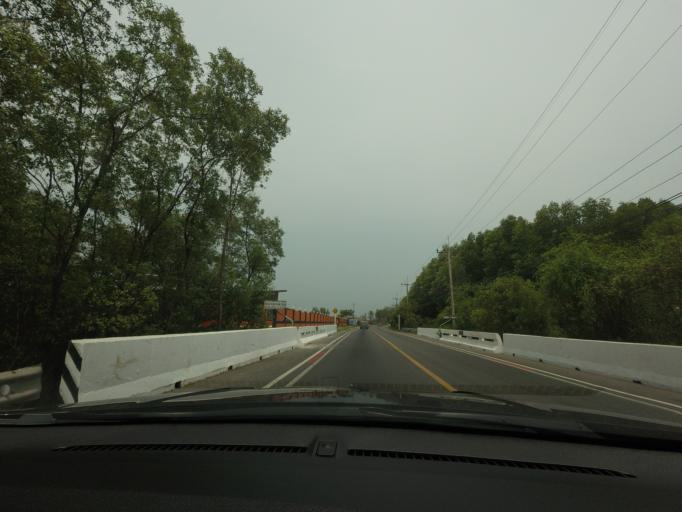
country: TH
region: Phetchaburi
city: Ban Laem
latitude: 13.2901
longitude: 99.9190
